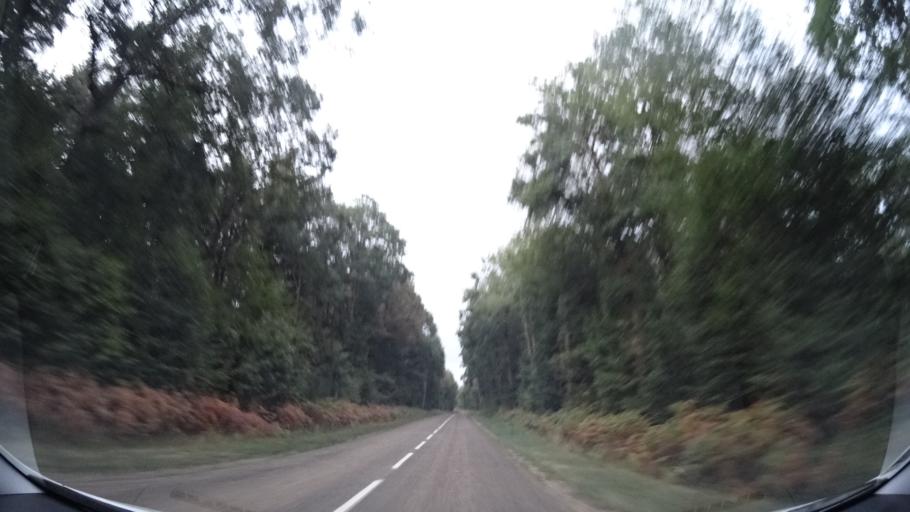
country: FR
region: Bourgogne
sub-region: Departement de l'Yonne
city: Aillant-sur-Tholon
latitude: 47.9269
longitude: 3.2835
